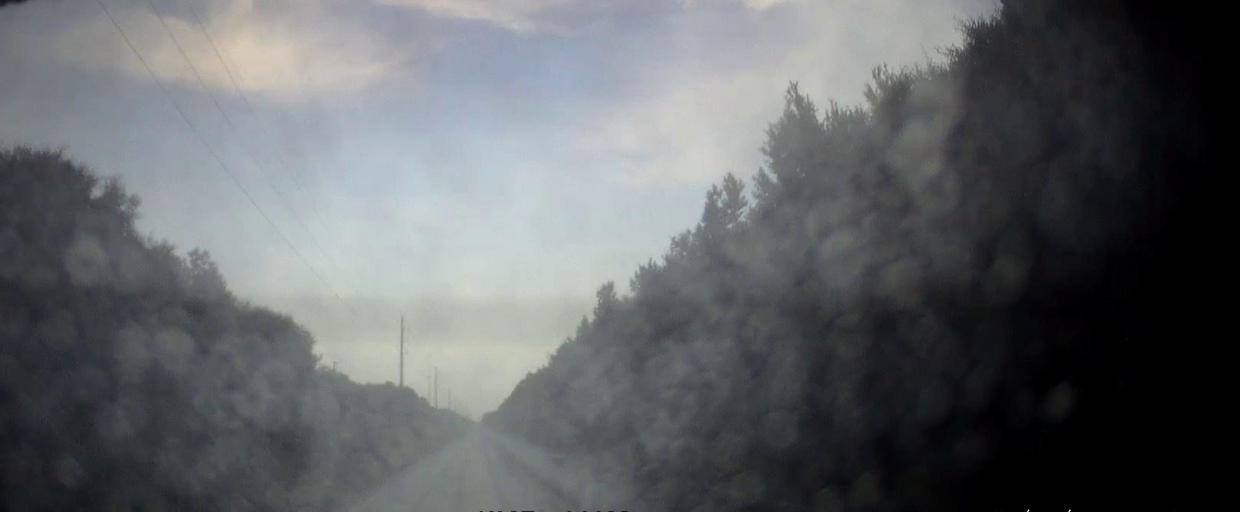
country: US
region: Georgia
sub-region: Dodge County
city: Chester
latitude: 32.5658
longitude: -83.1732
